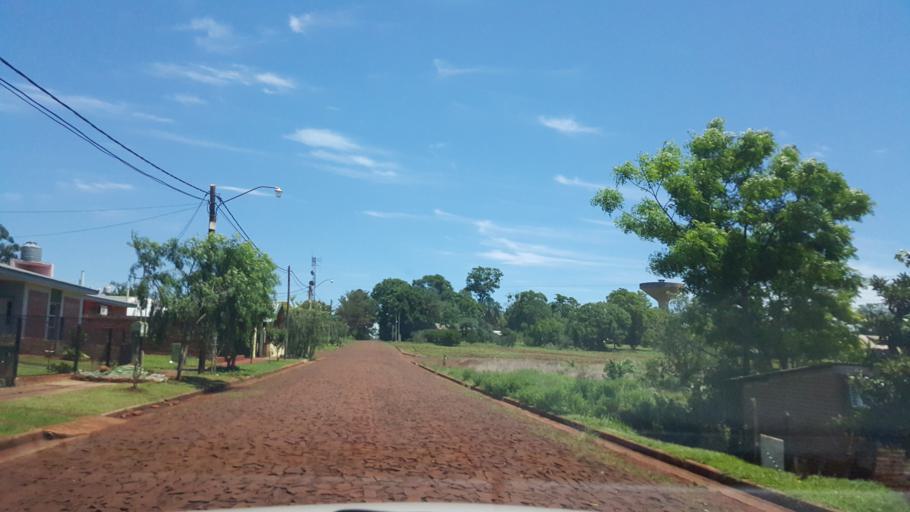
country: AR
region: Misiones
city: Capiovi
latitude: -26.9360
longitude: -55.0547
